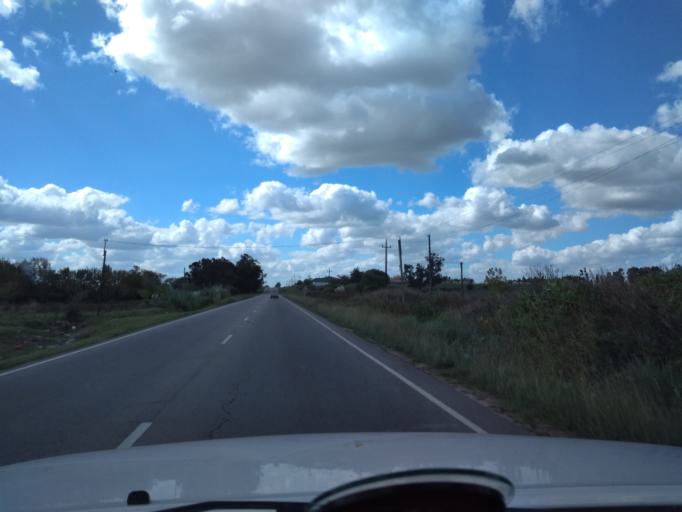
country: UY
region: Canelones
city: Joaquin Suarez
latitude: -34.6991
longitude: -56.0566
